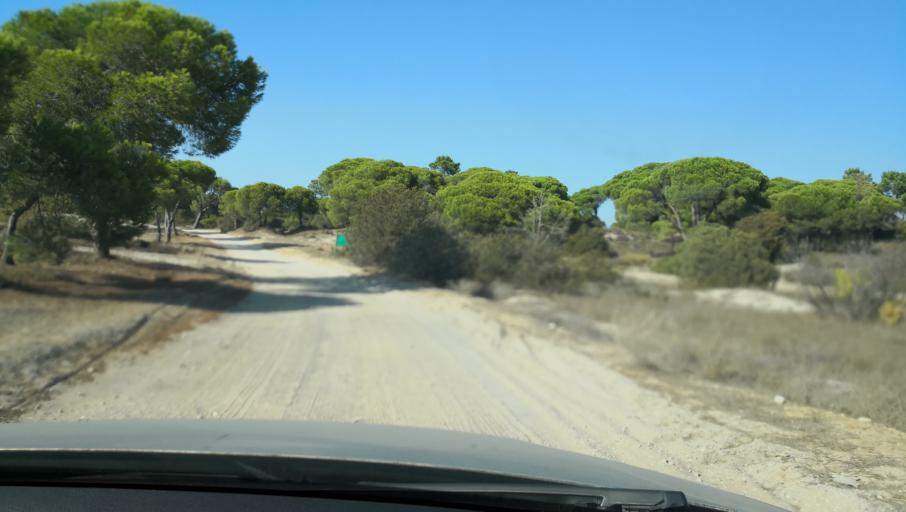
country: PT
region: Setubal
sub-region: Setubal
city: Setubal
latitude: 38.4828
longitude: -8.8813
